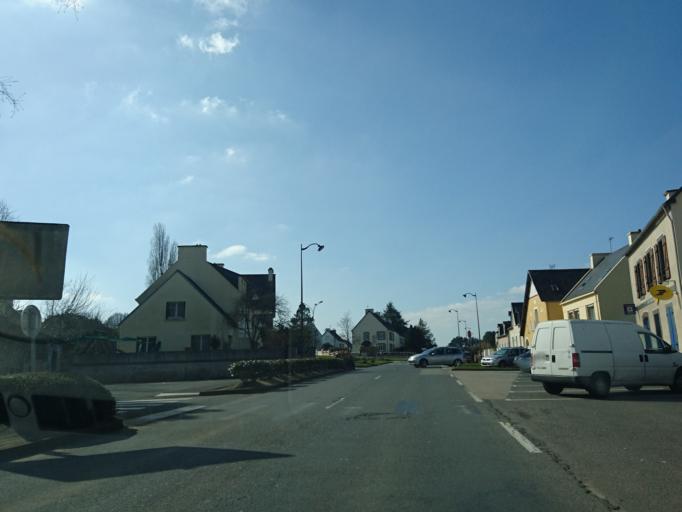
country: FR
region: Brittany
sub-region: Departement du Finistere
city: Le Faou
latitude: 48.2935
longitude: -4.1788
